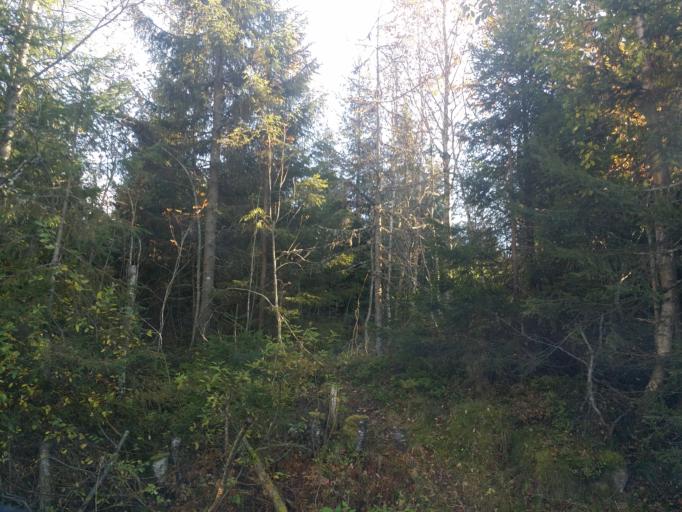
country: NO
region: Buskerud
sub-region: Hole
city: Vik
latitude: 60.0470
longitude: 10.3236
